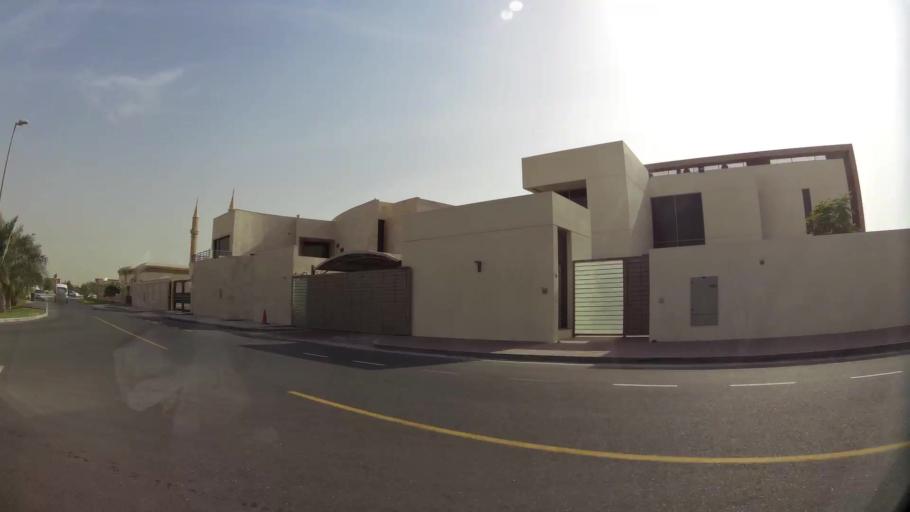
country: AE
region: Ash Shariqah
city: Sharjah
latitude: 25.2563
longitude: 55.4498
